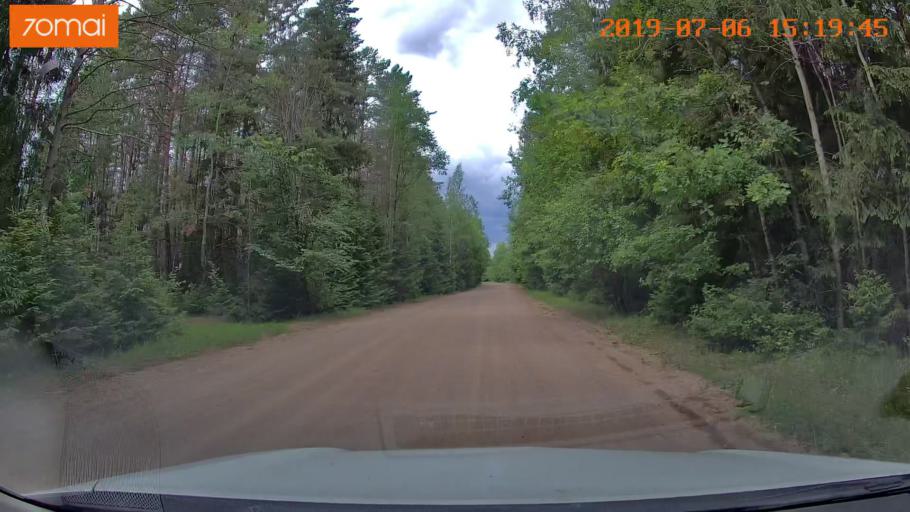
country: BY
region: Minsk
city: Valozhyn
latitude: 54.0004
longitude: 26.6439
